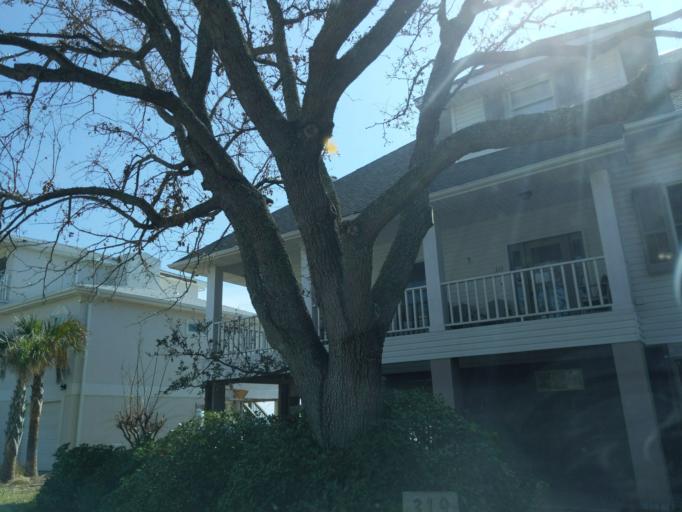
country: US
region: Florida
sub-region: Santa Rosa County
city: Gulf Breeze
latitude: 30.3508
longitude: -87.1890
